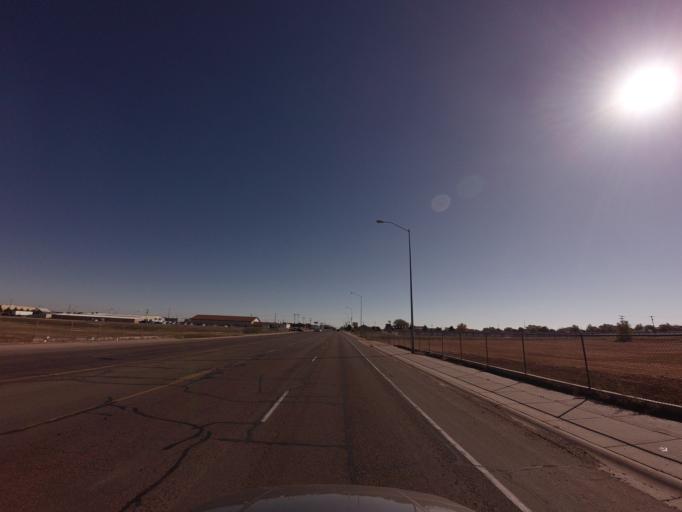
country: US
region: New Mexico
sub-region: Curry County
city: Clovis
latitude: 34.4339
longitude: -103.2032
